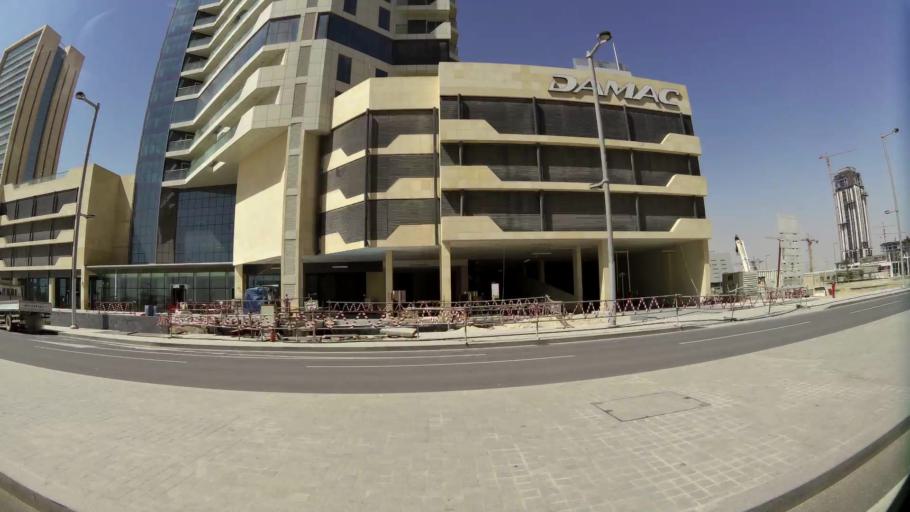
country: QA
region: Baladiyat ad Dawhah
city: Doha
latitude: 25.3910
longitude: 51.5226
